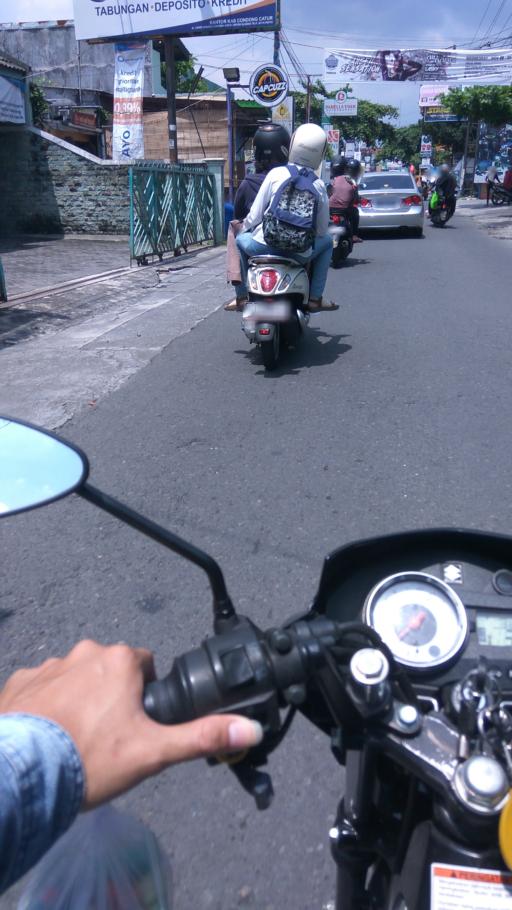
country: ID
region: Daerah Istimewa Yogyakarta
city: Depok
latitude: -7.7526
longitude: 110.4111
